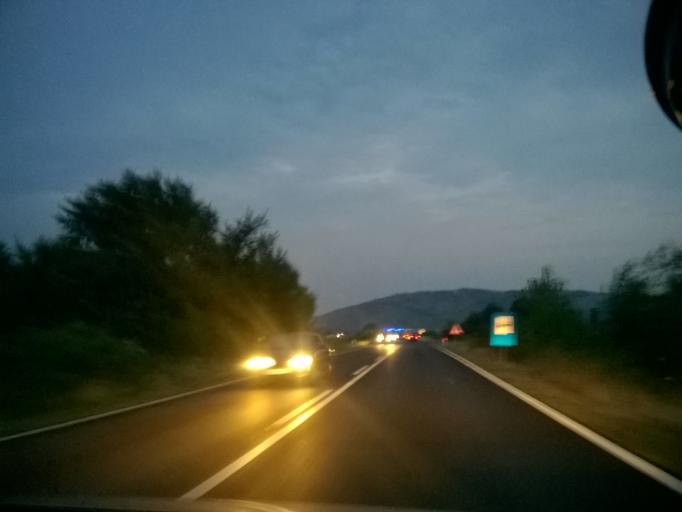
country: ME
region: Danilovgrad
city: Danilovgrad
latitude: 42.5176
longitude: 19.1229
